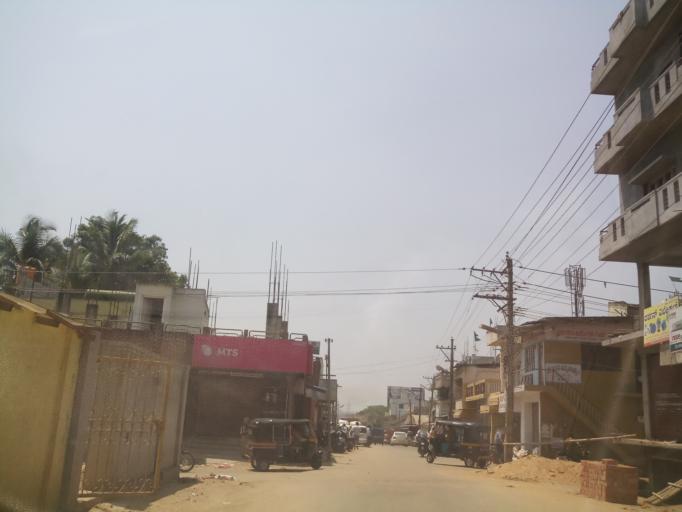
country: IN
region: Karnataka
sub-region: Hassan
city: Hassan
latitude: 13.0029
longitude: 76.0944
